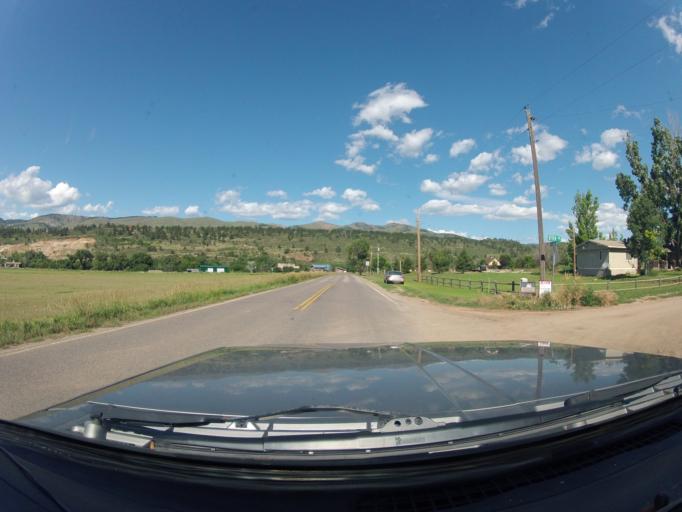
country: US
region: Colorado
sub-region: Larimer County
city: Laporte
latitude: 40.4873
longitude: -105.2122
